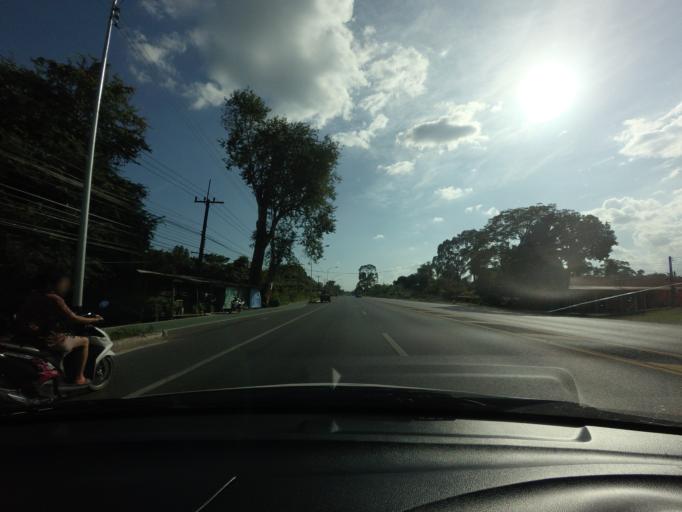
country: TH
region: Nakhon Nayok
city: Nakhon Nayok
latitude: 14.2799
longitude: 101.2755
